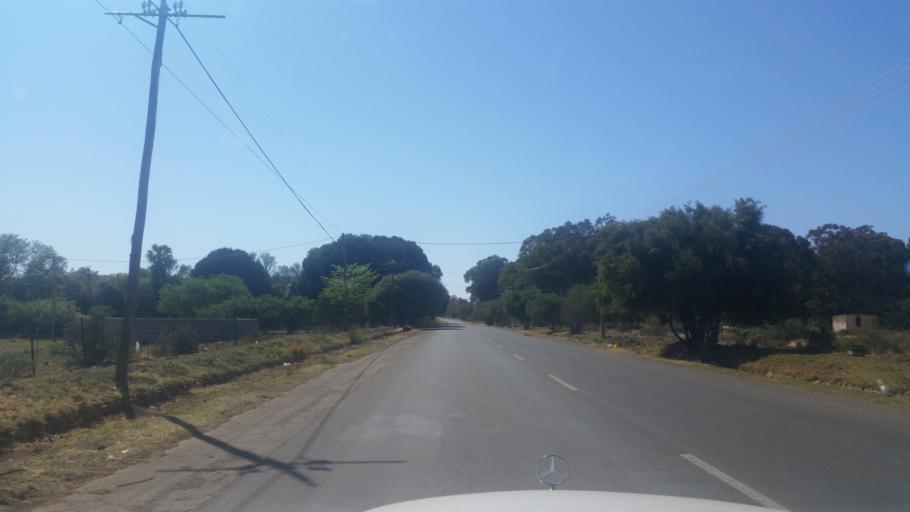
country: ZA
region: Orange Free State
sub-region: Xhariep District Municipality
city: Trompsburg
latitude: -30.4963
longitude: 25.9813
